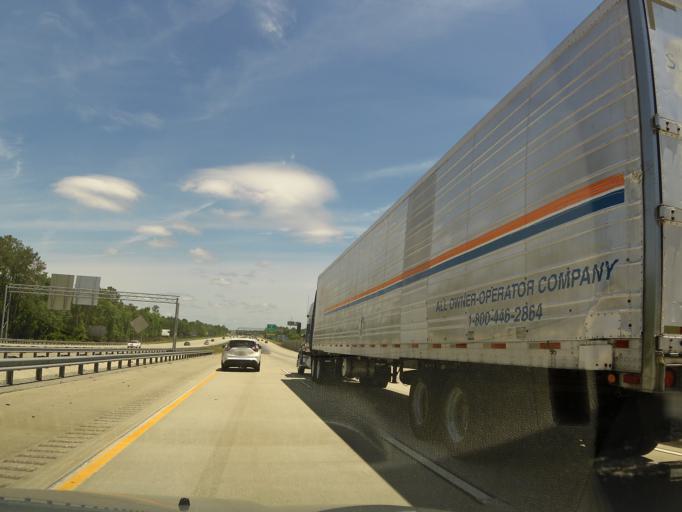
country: US
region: Georgia
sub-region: Glynn County
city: Dock Junction
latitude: 31.2291
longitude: -81.5146
